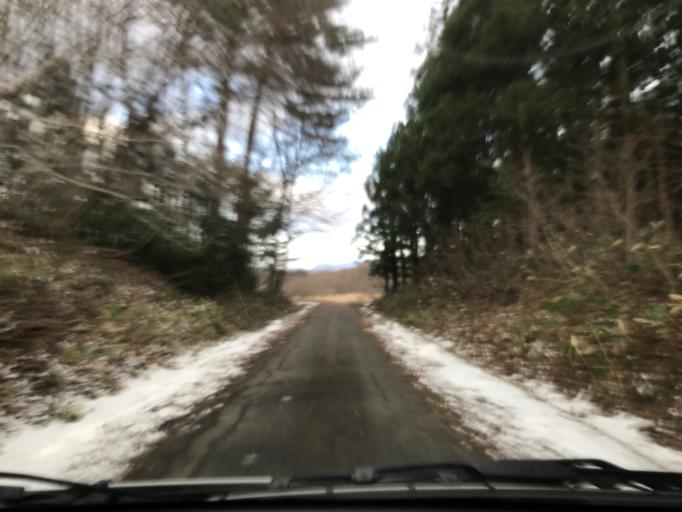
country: JP
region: Iwate
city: Ichinoseki
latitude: 38.9839
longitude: 141.0077
